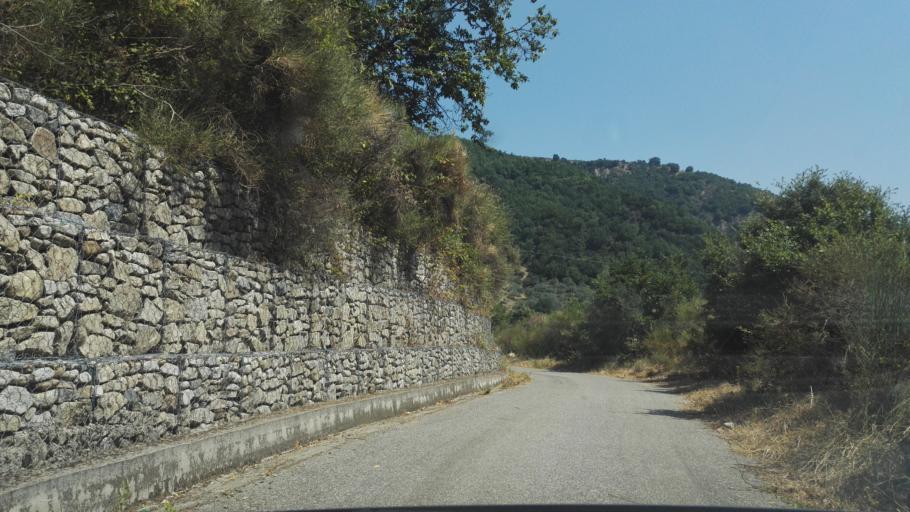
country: IT
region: Calabria
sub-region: Provincia di Reggio Calabria
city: Bivongi
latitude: 38.4887
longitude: 16.4210
